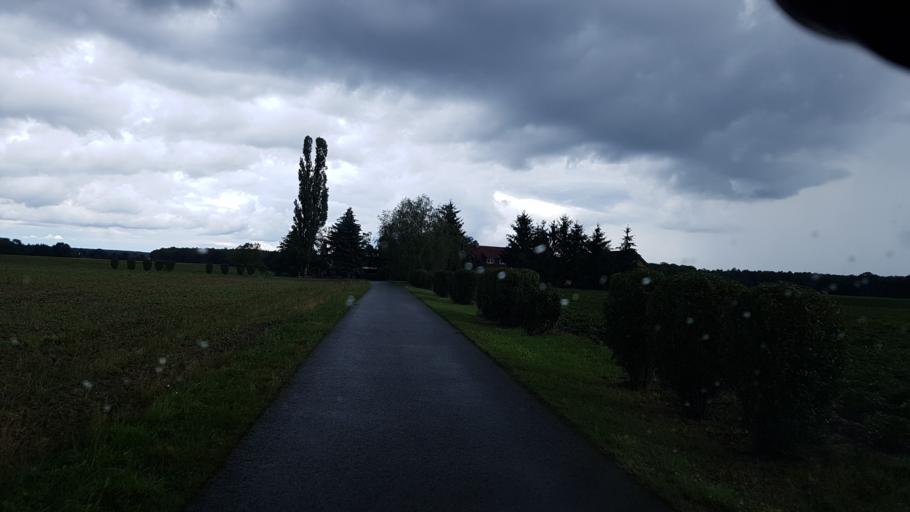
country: DE
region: Saxony
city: Gross Duben
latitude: 51.6309
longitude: 14.5282
